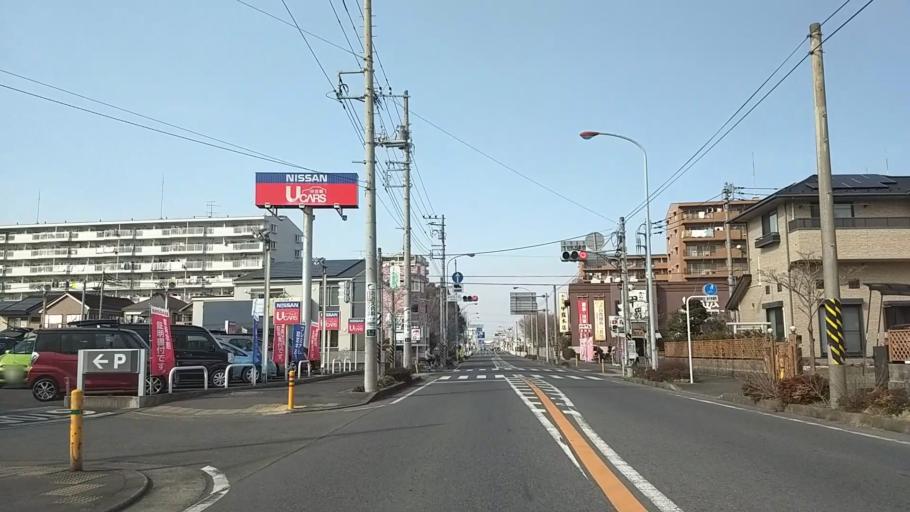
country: JP
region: Kanagawa
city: Chigasaki
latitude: 35.3384
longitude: 139.4137
